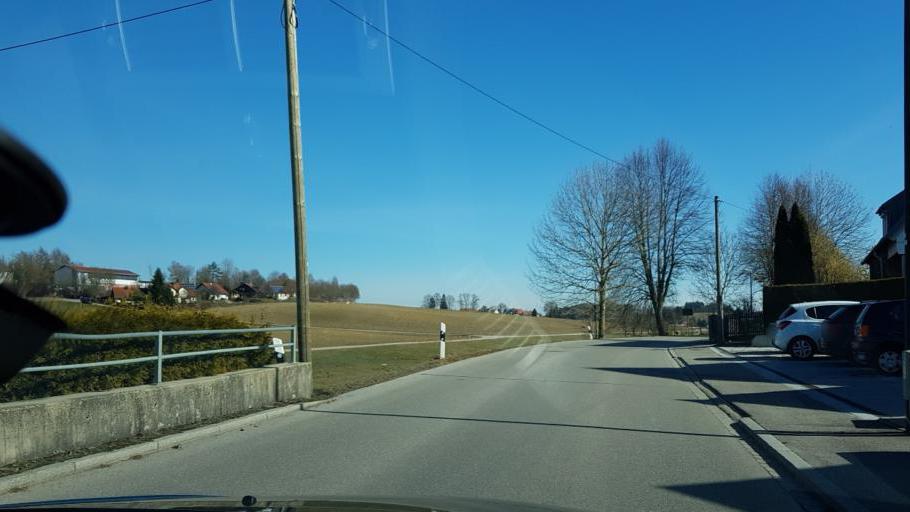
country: DE
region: Bavaria
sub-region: Upper Bavaria
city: Oberschweinbach
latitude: 48.2413
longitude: 11.1453
